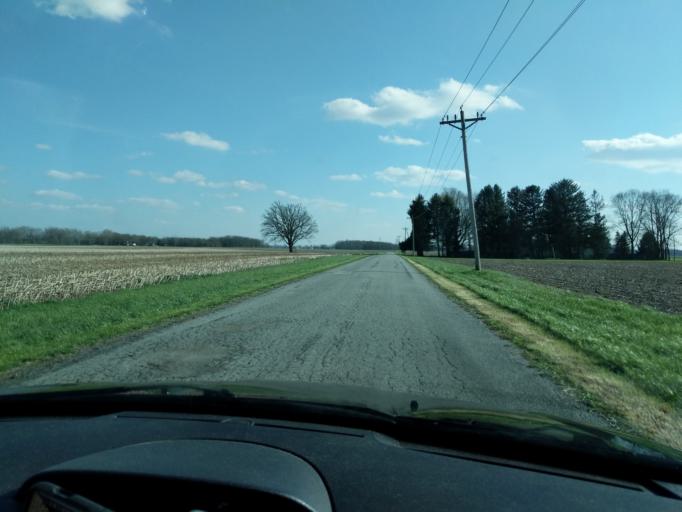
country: US
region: Ohio
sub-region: Champaign County
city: Urbana
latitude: 40.1414
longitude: -83.8155
